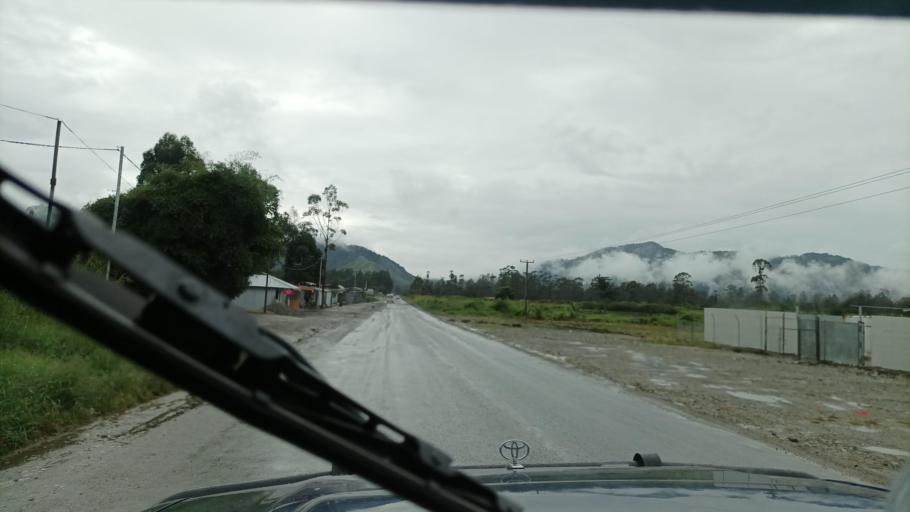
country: PG
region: Western Highlands
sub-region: Hagen
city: Mount Hagen
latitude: -5.8376
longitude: 144.3290
